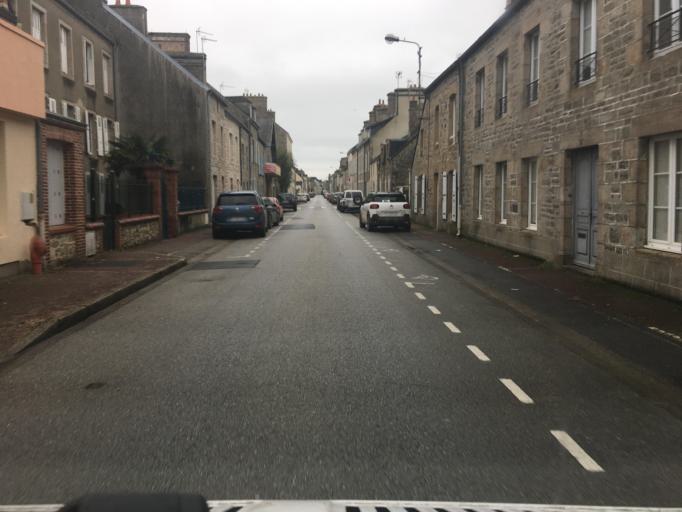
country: FR
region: Lower Normandy
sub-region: Departement de la Manche
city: Saint-Vaast-la-Hougue
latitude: 49.5872
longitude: -1.2706
